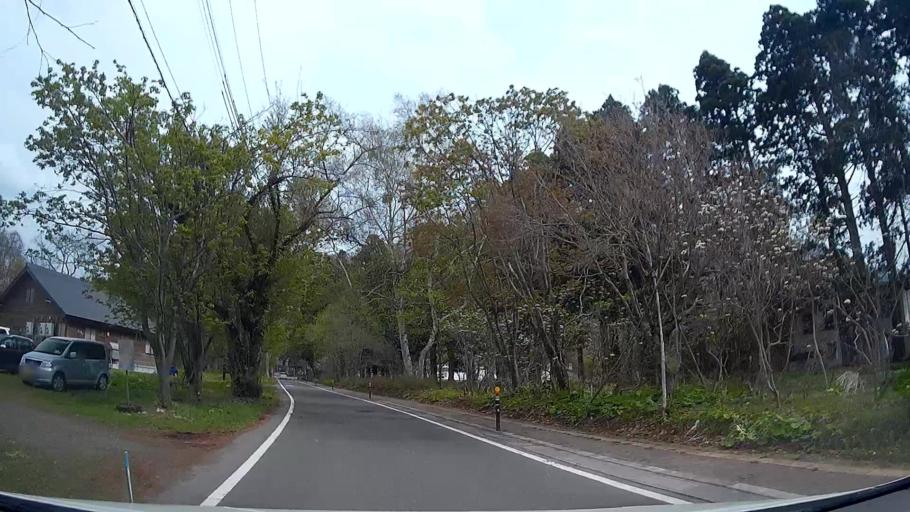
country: JP
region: Akita
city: Hanawa
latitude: 40.4267
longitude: 140.8954
